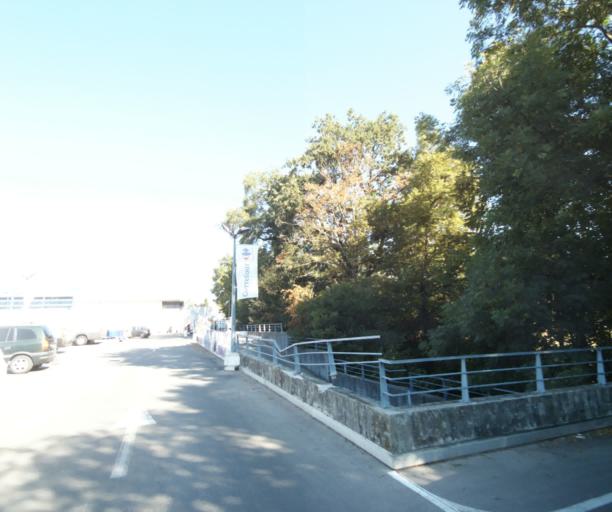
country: FR
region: Rhone-Alpes
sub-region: Departement de l'Ain
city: Ferney-Voltaire
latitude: 46.2537
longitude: 6.1212
